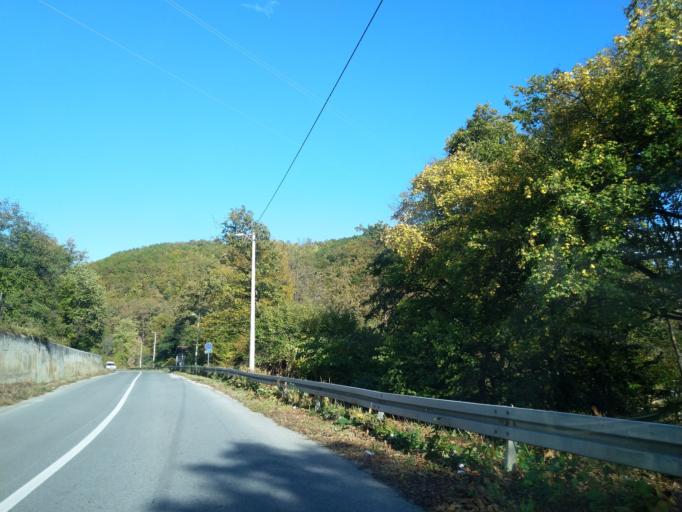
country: RS
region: Central Serbia
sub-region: Zlatiborski Okrug
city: Uzice
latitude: 43.8647
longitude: 19.8119
